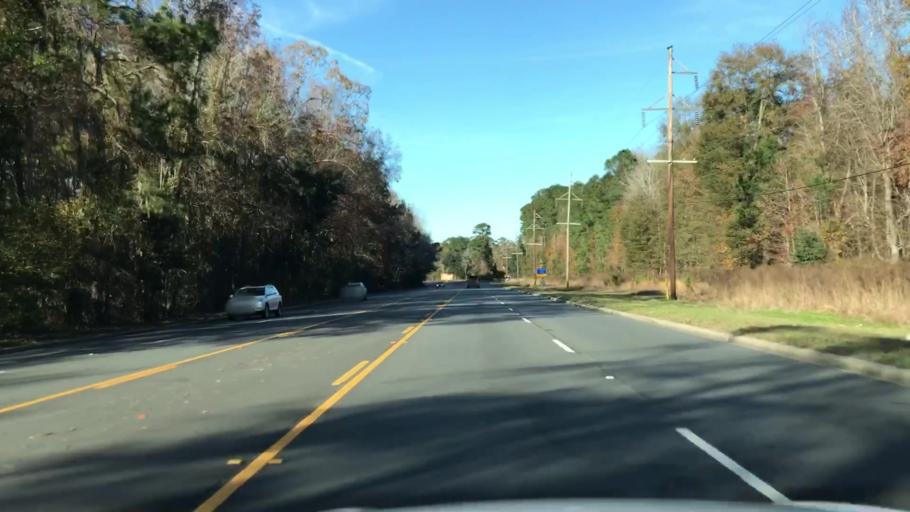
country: US
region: South Carolina
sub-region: Beaufort County
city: Laurel Bay
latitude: 32.5810
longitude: -80.7430
